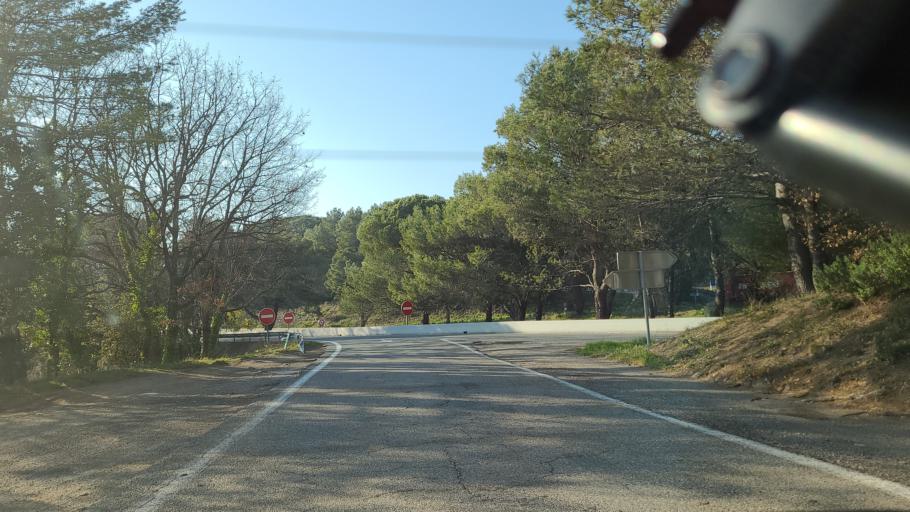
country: FR
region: Provence-Alpes-Cote d'Azur
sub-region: Departement du Var
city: Cabasse
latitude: 43.4042
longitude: 6.1993
